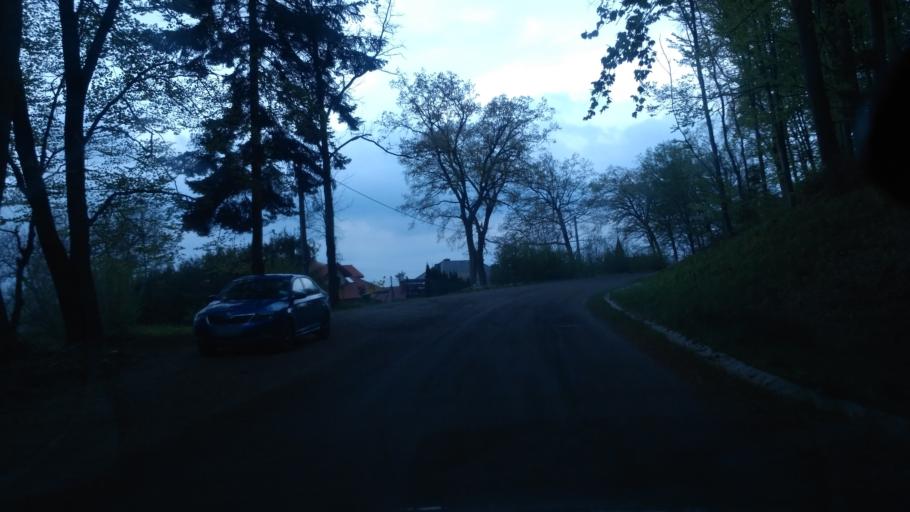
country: PL
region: Subcarpathian Voivodeship
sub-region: Powiat sanocki
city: Sanok
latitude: 49.5718
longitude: 22.2258
